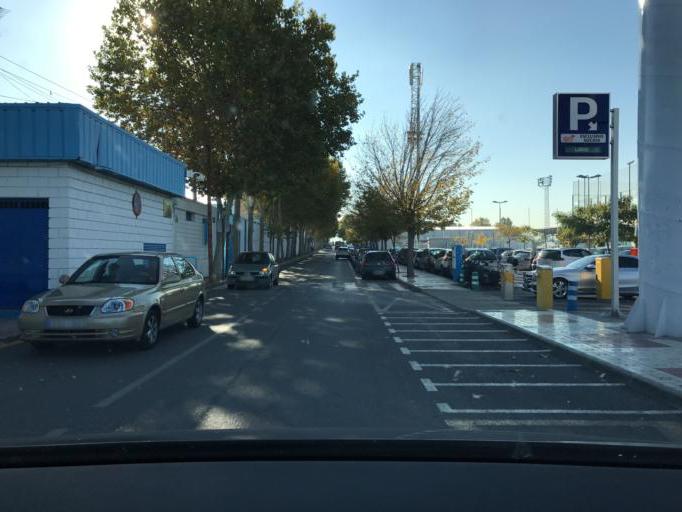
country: ES
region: Andalusia
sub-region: Provincia de Granada
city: Maracena
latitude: 37.2116
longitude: -3.6287
